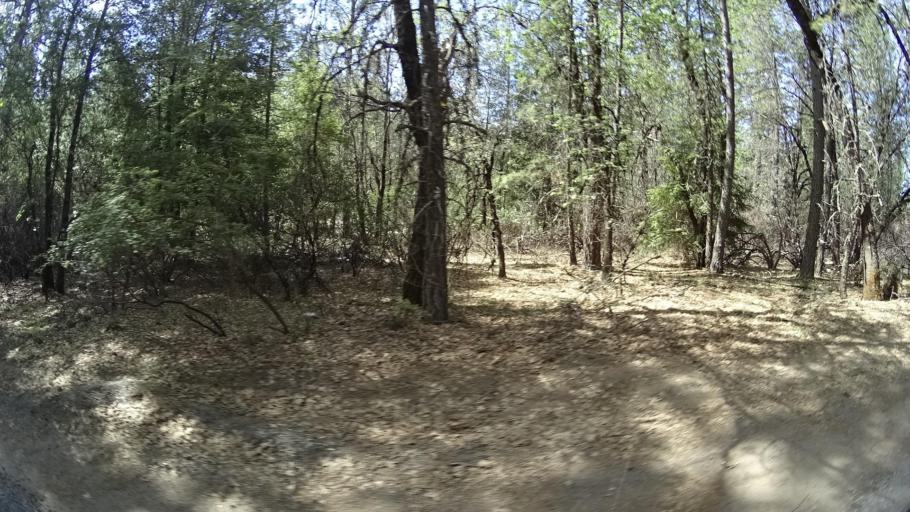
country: US
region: California
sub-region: Lake County
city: Cobb
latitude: 38.8708
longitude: -122.7603
